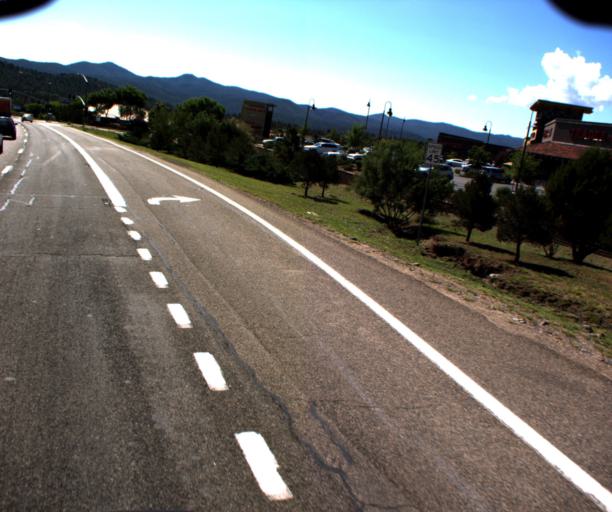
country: US
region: Arizona
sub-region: Yavapai County
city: Prescott
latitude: 34.5495
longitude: -112.4056
